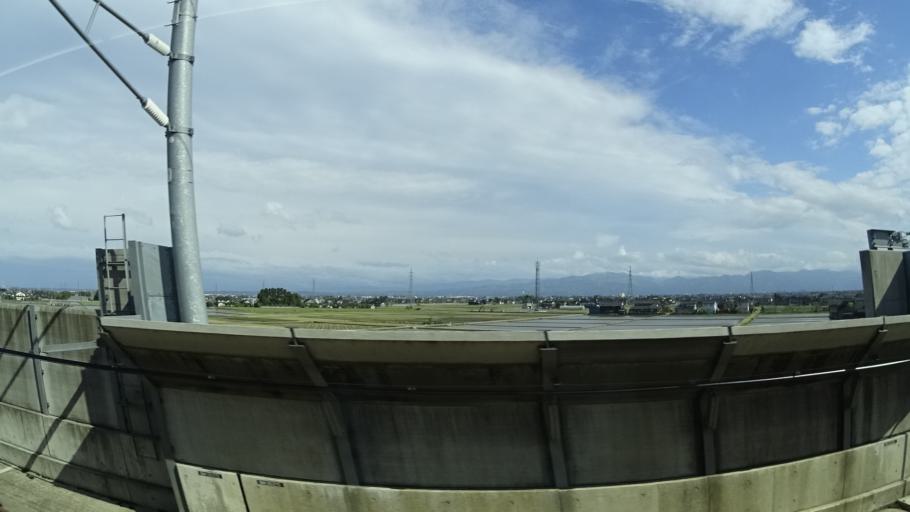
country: JP
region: Toyama
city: Takaoka
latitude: 36.7059
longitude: 136.9487
